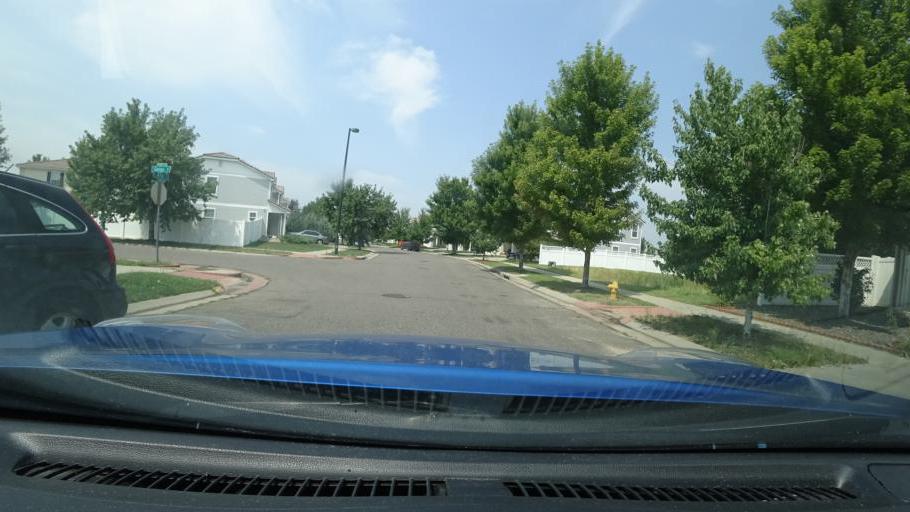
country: US
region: Colorado
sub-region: Adams County
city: Aurora
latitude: 39.7833
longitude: -104.7589
